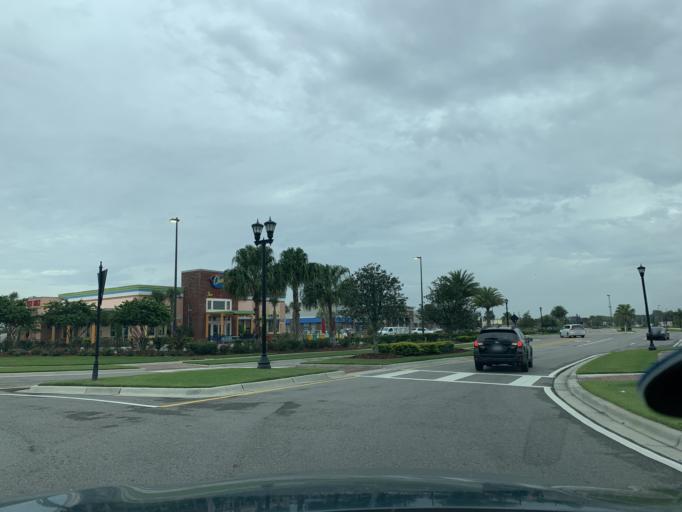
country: US
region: Florida
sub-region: Hillsborough County
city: Pebble Creek
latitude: 28.1962
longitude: -82.3909
